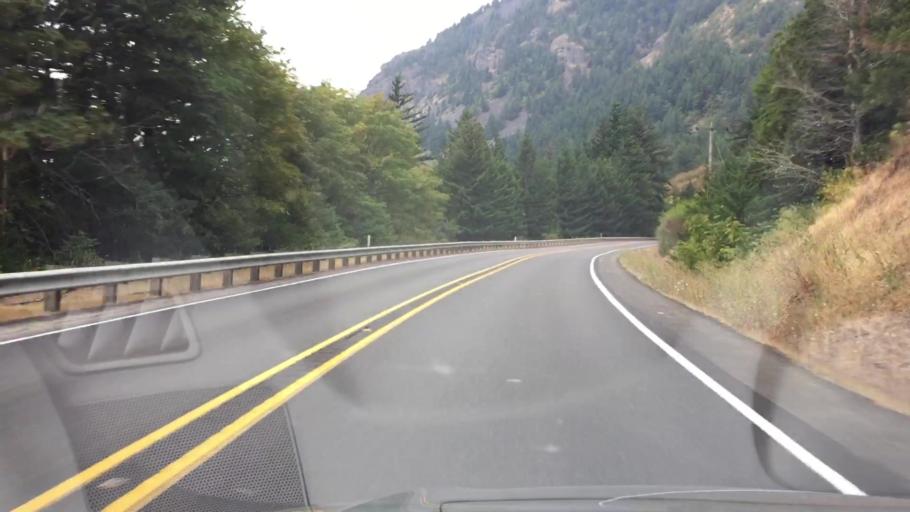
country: US
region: Washington
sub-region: Skamania County
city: Carson
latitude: 45.6995
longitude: -121.7388
